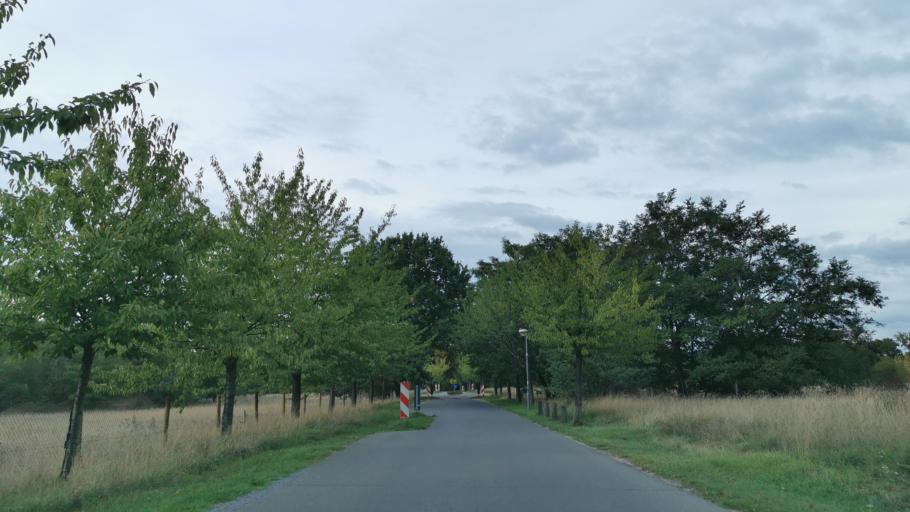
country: DE
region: Brandenburg
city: Werder
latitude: 52.3577
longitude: 12.9482
